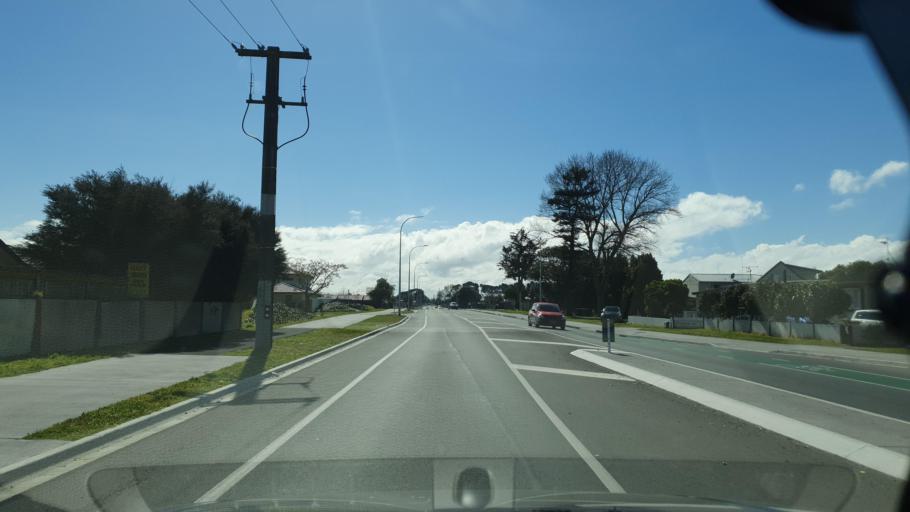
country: NZ
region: Bay of Plenty
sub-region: Tauranga City
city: Tauranga
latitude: -37.7068
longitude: 176.2847
